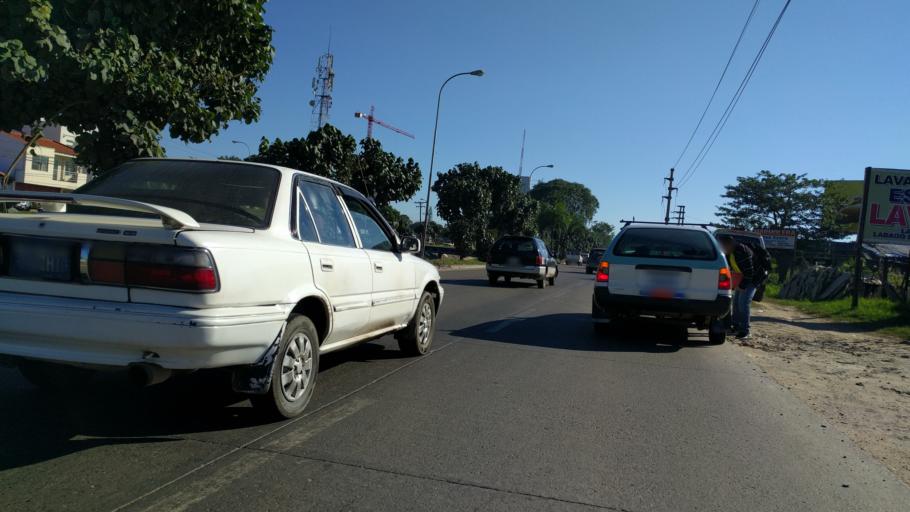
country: BO
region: Santa Cruz
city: Santa Cruz de la Sierra
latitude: -17.7881
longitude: -63.2165
